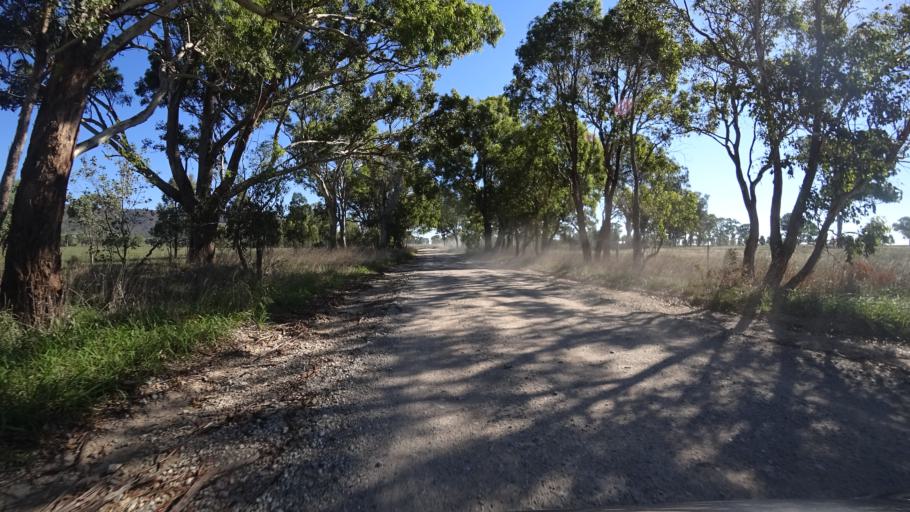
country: AU
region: New South Wales
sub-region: Mid-Western Regional
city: Kandos
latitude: -32.8285
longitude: 150.0175
